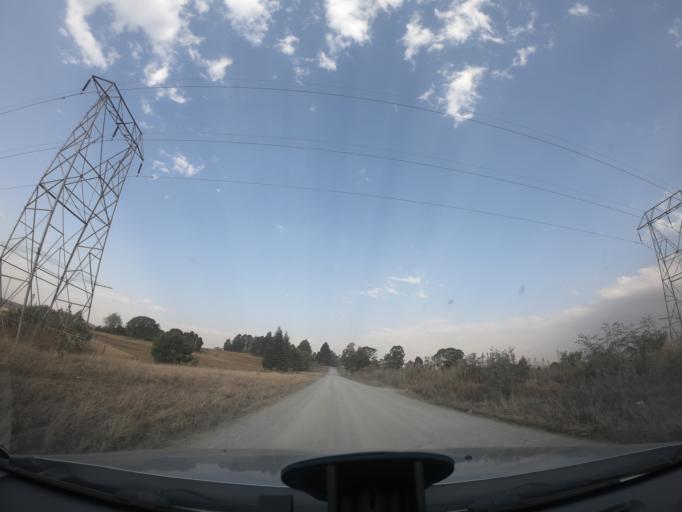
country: ZA
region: KwaZulu-Natal
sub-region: uMgungundlovu District Municipality
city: Howick
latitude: -29.4331
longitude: 30.1115
